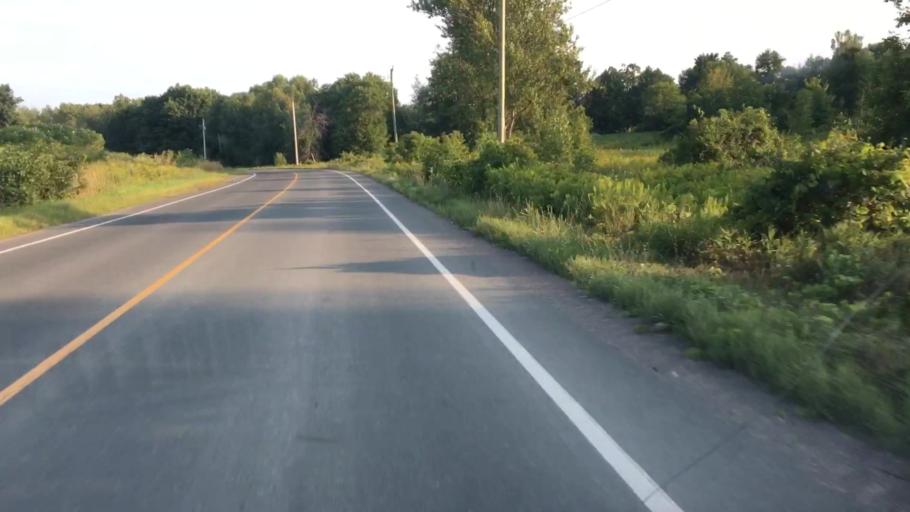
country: CA
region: Ontario
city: Quinte West
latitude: 44.0971
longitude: -77.7354
